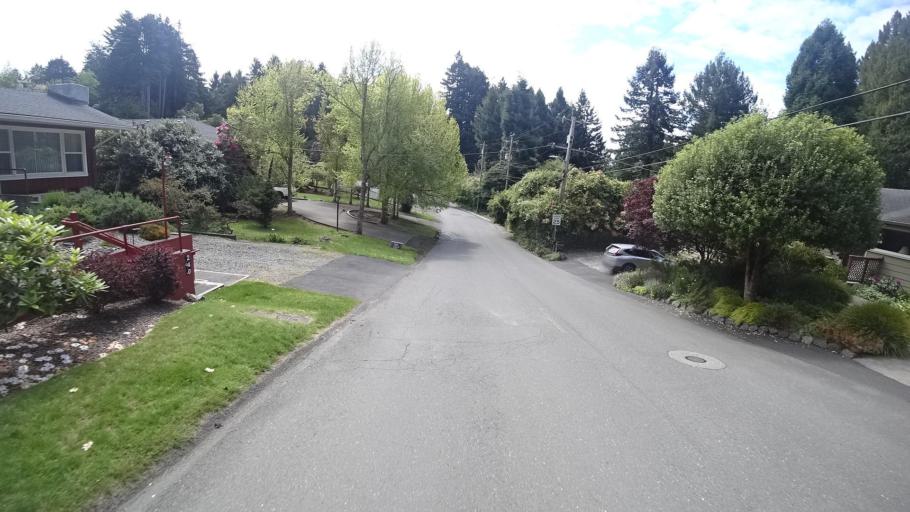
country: US
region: California
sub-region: Humboldt County
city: Arcata
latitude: 40.8678
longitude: -124.0711
